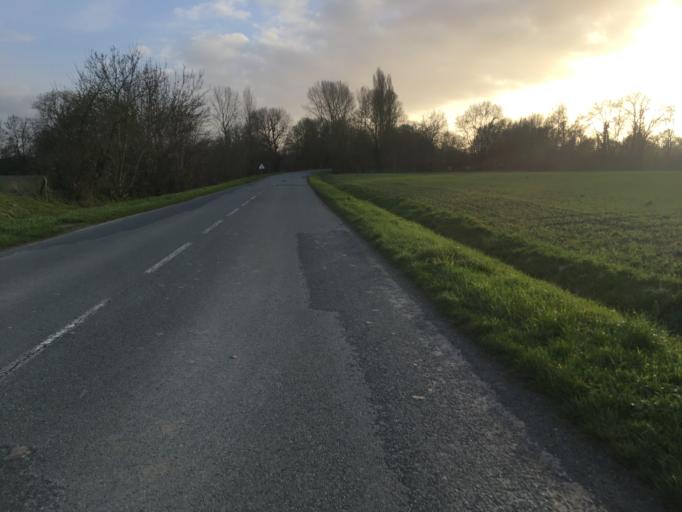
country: FR
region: Poitou-Charentes
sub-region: Departement de la Charente-Maritime
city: Courcon
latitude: 46.1702
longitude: -0.8493
